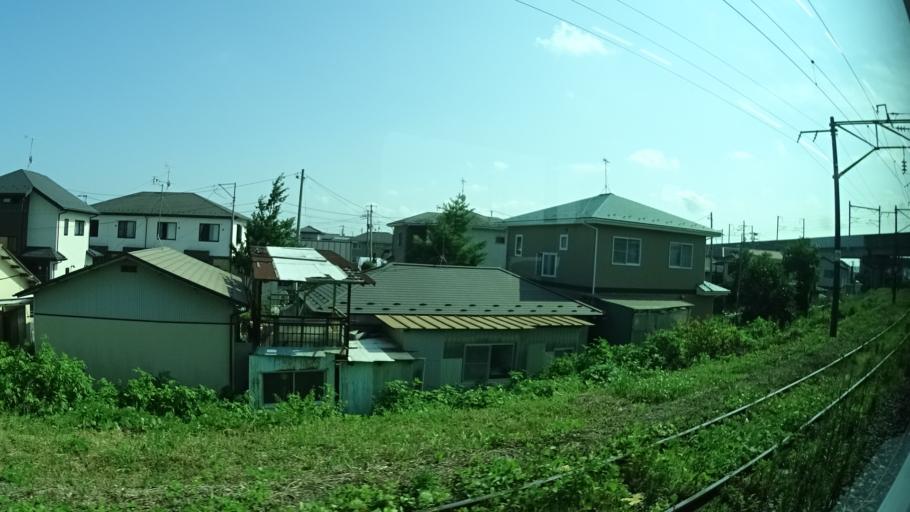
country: JP
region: Miyagi
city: Rifu
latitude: 38.3014
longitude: 140.9583
